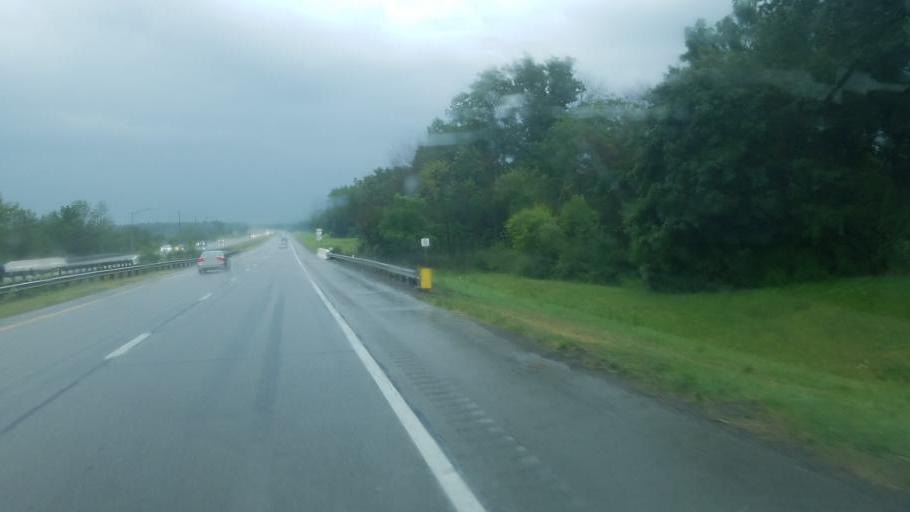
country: US
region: Ohio
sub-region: Trumbull County
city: Champion Heights
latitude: 41.2757
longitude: -80.8382
